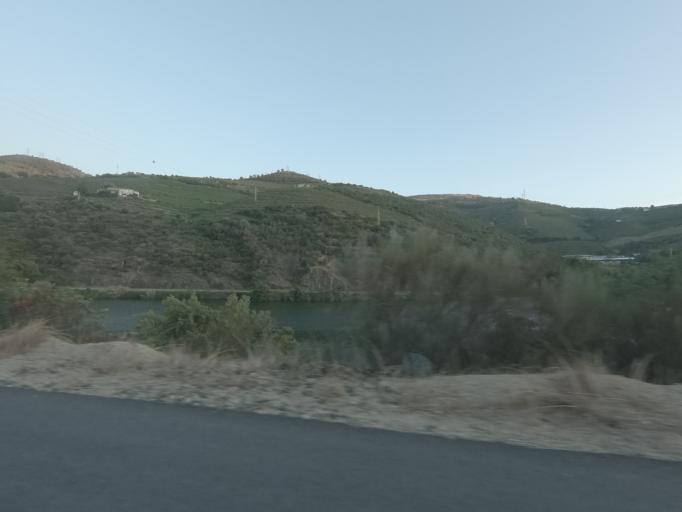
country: PT
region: Viseu
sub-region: Armamar
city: Armamar
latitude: 41.1465
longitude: -7.7308
